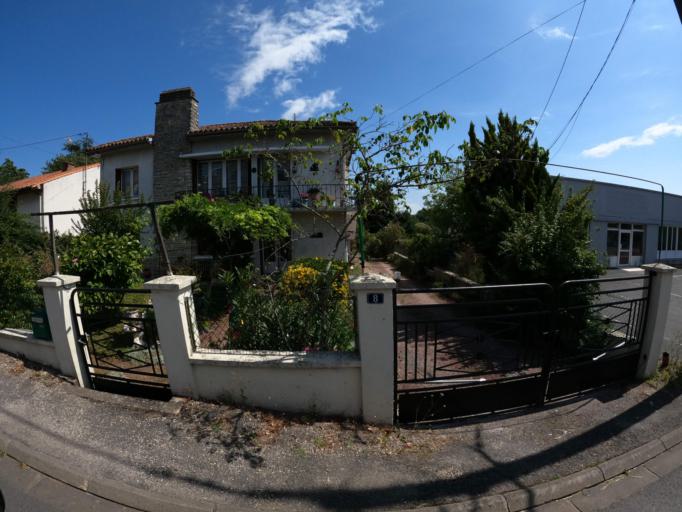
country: FR
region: Poitou-Charentes
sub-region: Departement de la Vienne
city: Civray
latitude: 46.1514
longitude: 0.2961
